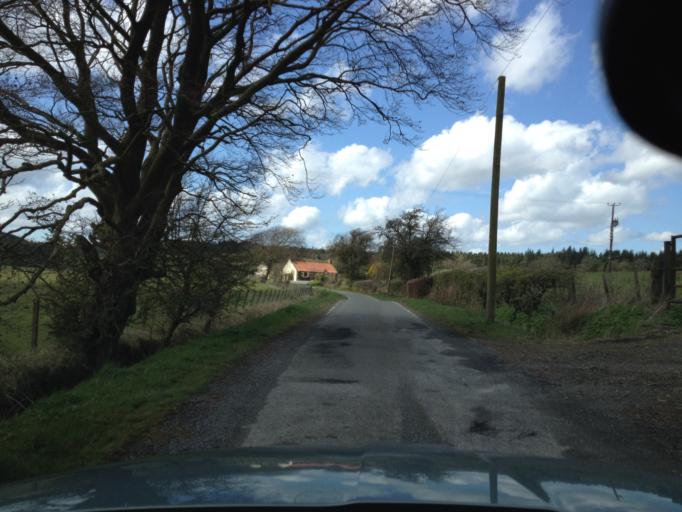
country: GB
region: Scotland
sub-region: West Lothian
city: Linlithgow
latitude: 55.9395
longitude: -3.5835
